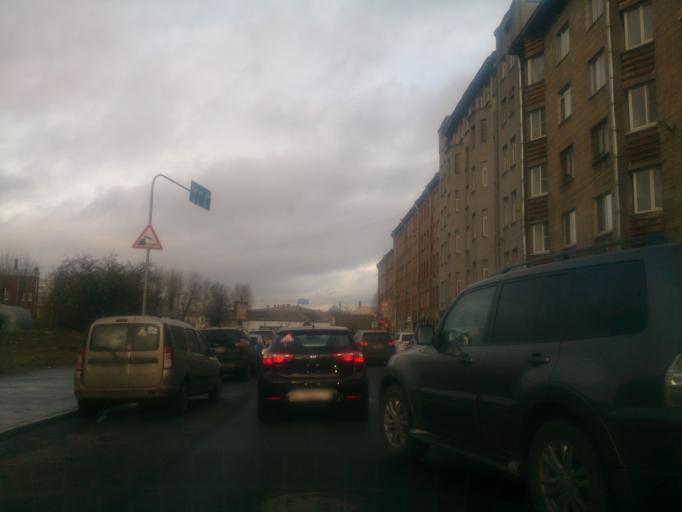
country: RU
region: St.-Petersburg
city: Admiralteisky
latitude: 59.9076
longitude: 30.2948
